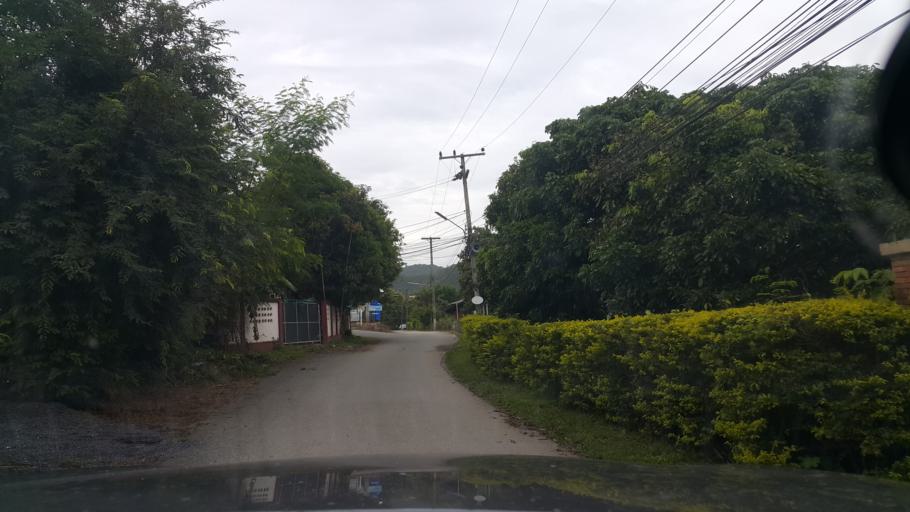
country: TH
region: Chiang Mai
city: Mae On
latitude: 18.8360
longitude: 99.1846
